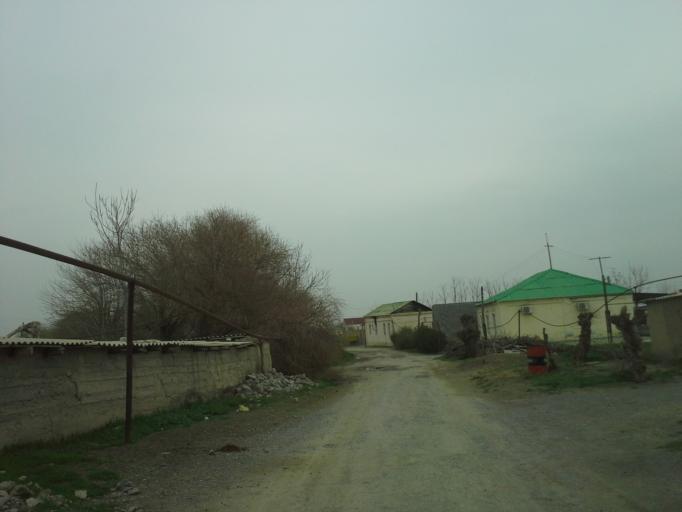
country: TM
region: Ahal
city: Abadan
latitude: 37.9684
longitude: 58.2212
